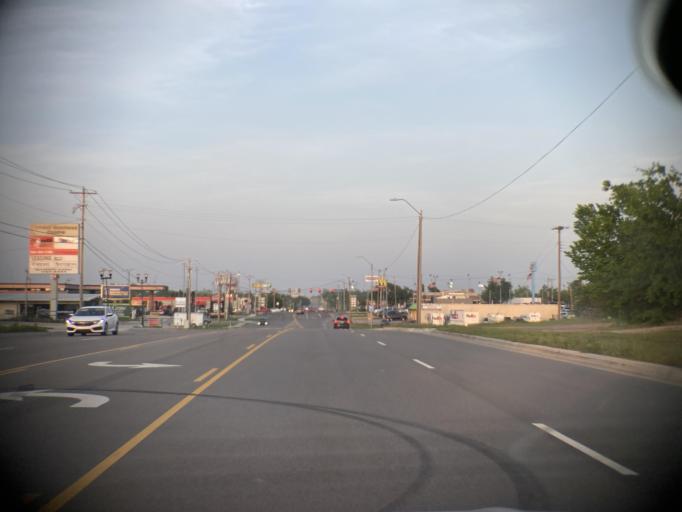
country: US
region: Oklahoma
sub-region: Oklahoma County
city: Midwest City
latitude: 35.4352
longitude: -97.3742
